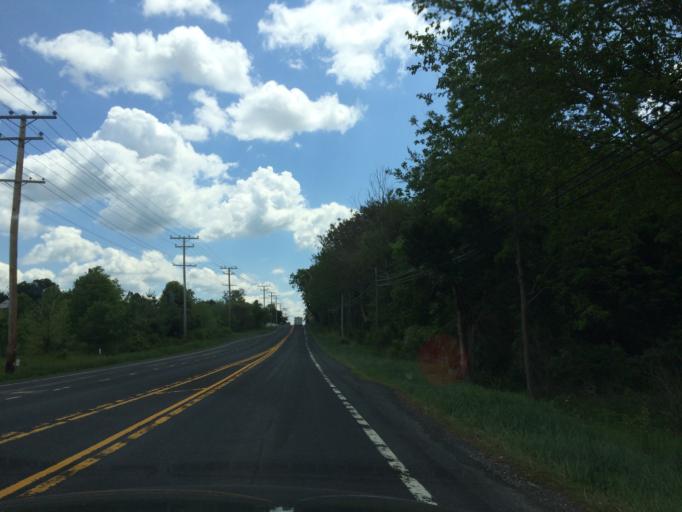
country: US
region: Maryland
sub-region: Carroll County
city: Sykesville
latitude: 39.3158
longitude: -77.0021
